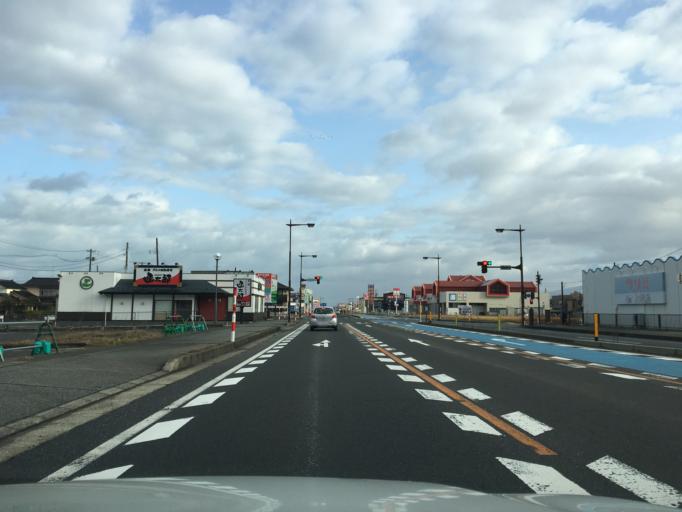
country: JP
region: Yamagata
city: Sakata
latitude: 38.9155
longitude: 139.8581
